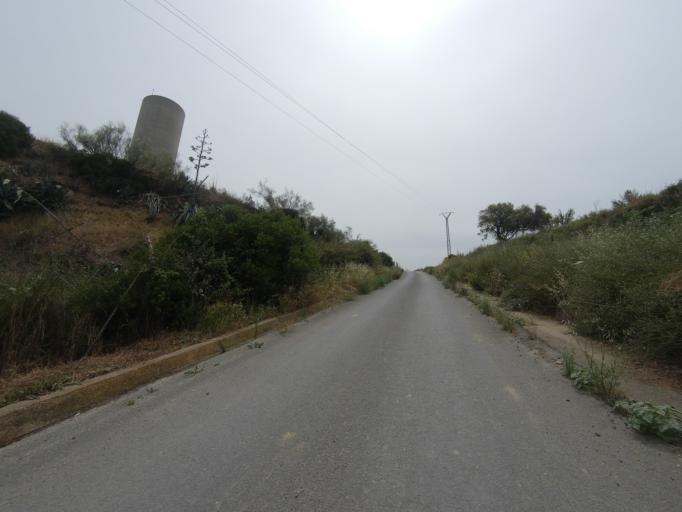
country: ES
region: Andalusia
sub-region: Provincia de Huelva
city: Palos de la Frontera
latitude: 37.2430
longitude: -6.8864
